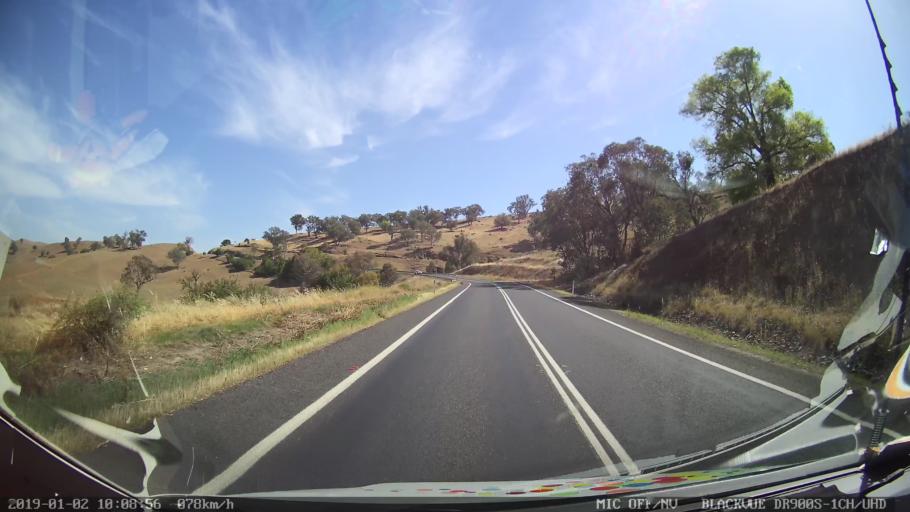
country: AU
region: New South Wales
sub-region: Gundagai
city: Gundagai
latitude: -35.1218
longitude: 148.1008
